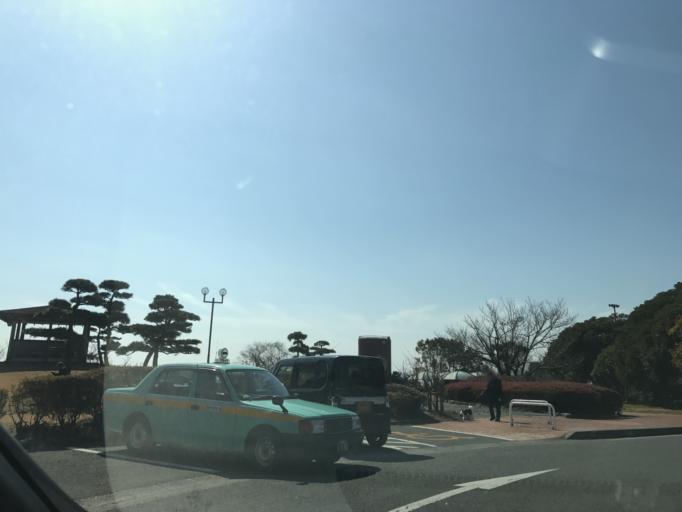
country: JP
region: Fukushima
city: Iwaki
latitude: 36.9355
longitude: 140.9211
